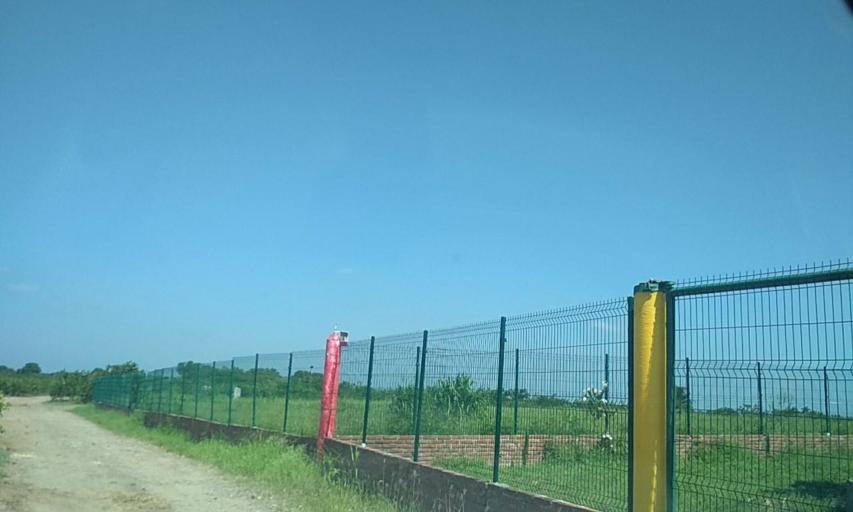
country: MX
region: Veracruz
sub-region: Martinez de la Torre
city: La Union Paso Largo
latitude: 20.1523
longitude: -96.9954
